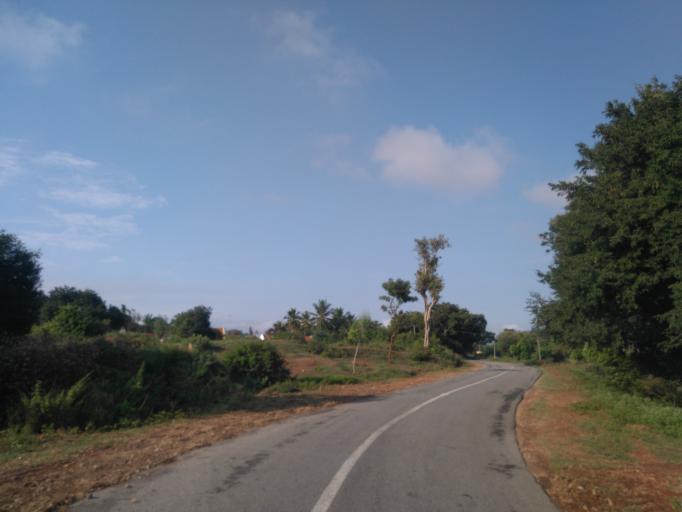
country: IN
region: Karnataka
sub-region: Mandya
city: Malavalli
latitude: 12.3225
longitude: 77.0738
